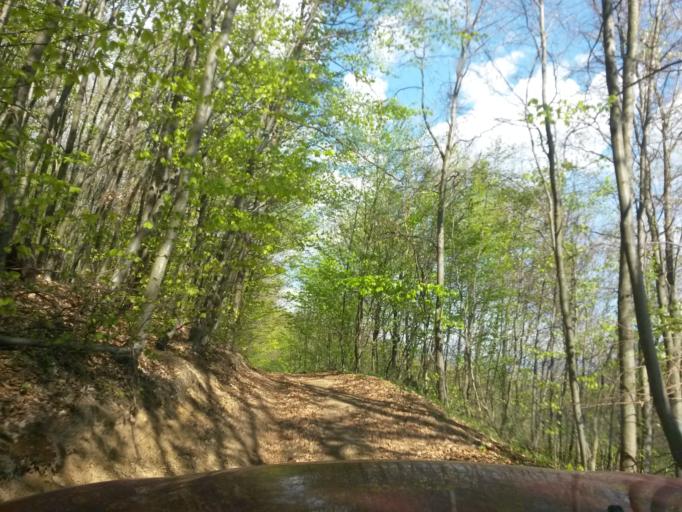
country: SK
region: Presovsky
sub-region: Okres Presov
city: Presov
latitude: 48.9498
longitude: 21.1377
